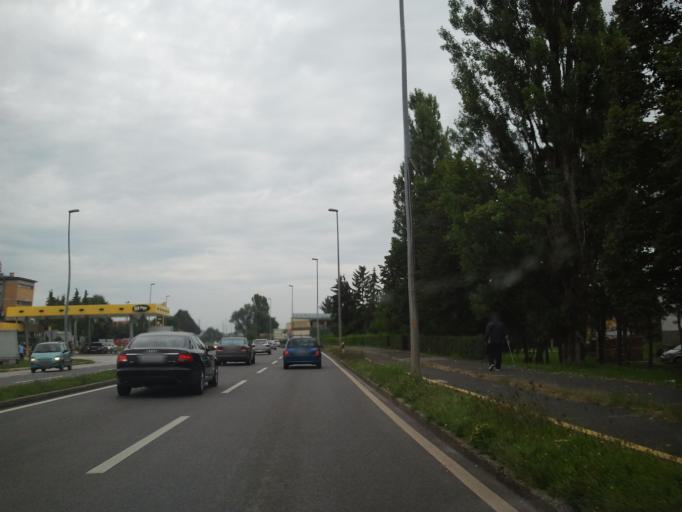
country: HR
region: Karlovacka
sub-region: Grad Karlovac
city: Karlovac
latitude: 45.5006
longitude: 15.5459
